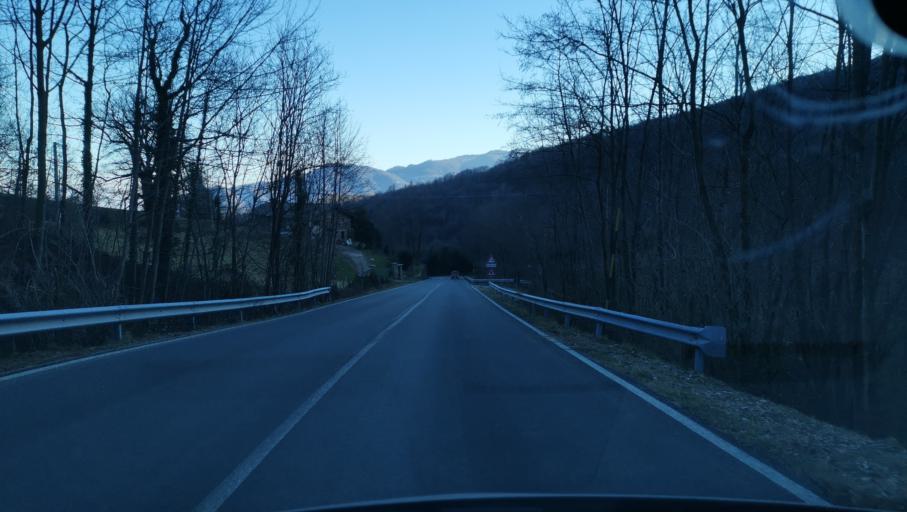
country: IT
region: Piedmont
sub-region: Provincia di Cuneo
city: Bagnolo Piemonte
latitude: 44.7513
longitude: 7.2652
